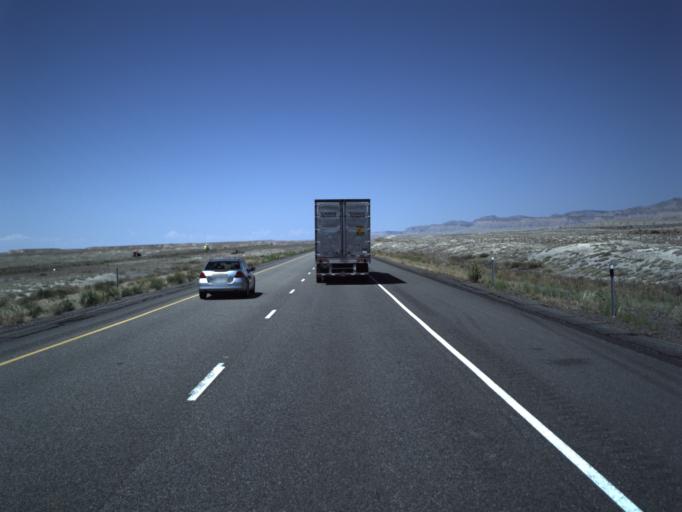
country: US
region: Utah
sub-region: Grand County
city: Moab
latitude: 38.9354
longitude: -109.4571
